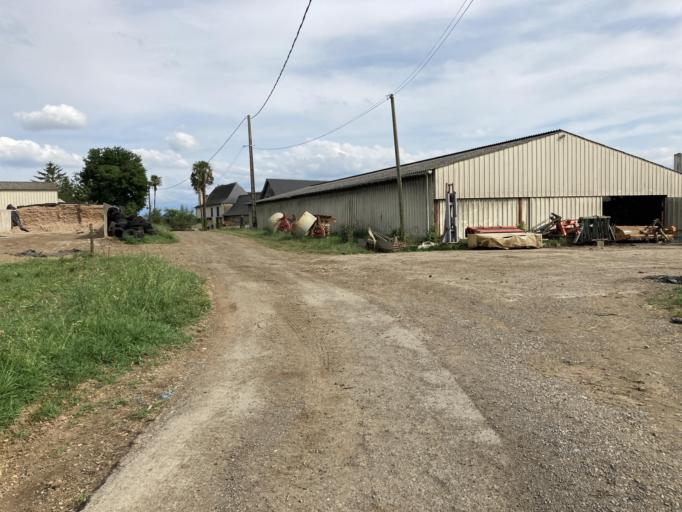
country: FR
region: Aquitaine
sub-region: Departement des Pyrenees-Atlantiques
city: Ledeuix
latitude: 43.2731
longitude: -0.6061
